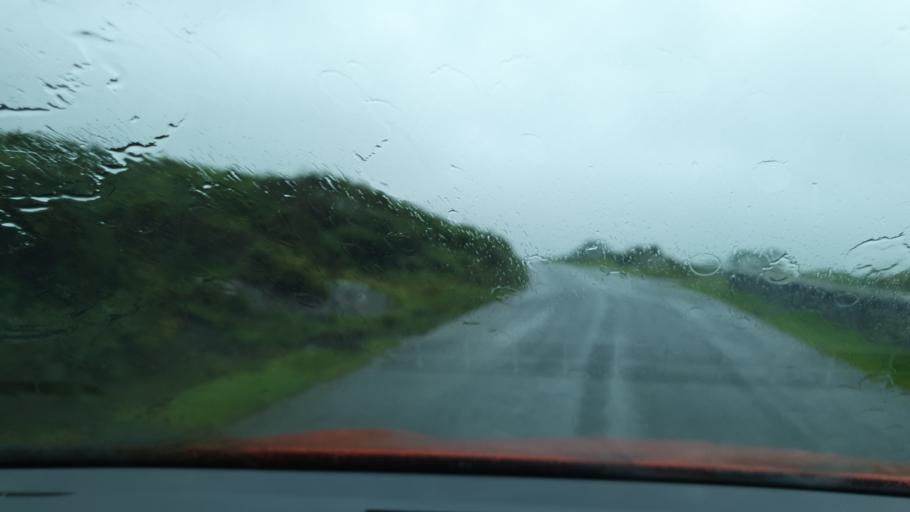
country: GB
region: England
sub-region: Cumbria
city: Millom
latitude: 54.3250
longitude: -3.2362
